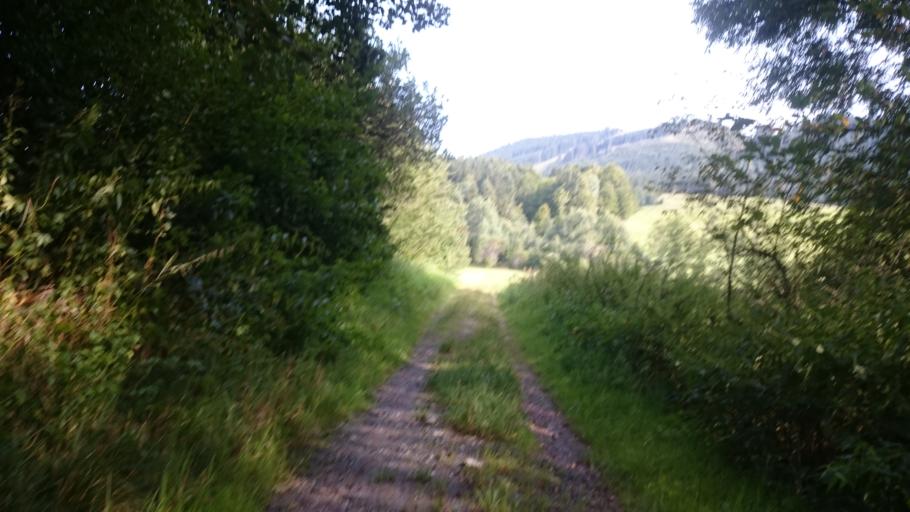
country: DE
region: Bavaria
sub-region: Swabia
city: Oy-Mittelberg
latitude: 47.6080
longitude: 10.4427
